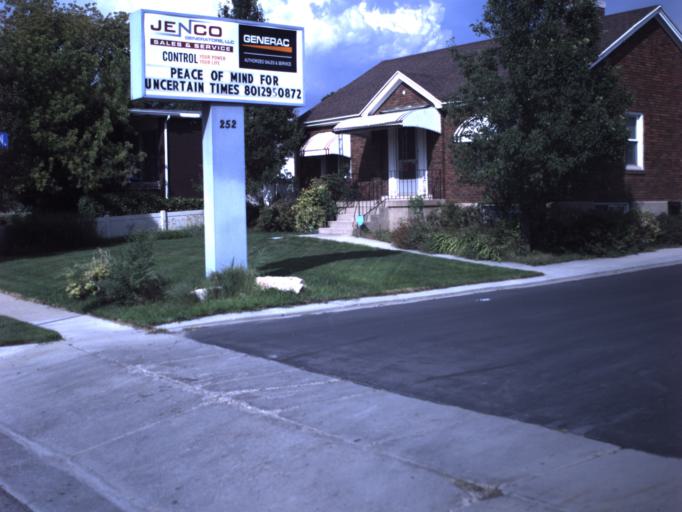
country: US
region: Utah
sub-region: Davis County
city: North Salt Lake
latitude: 40.8461
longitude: -111.9079
